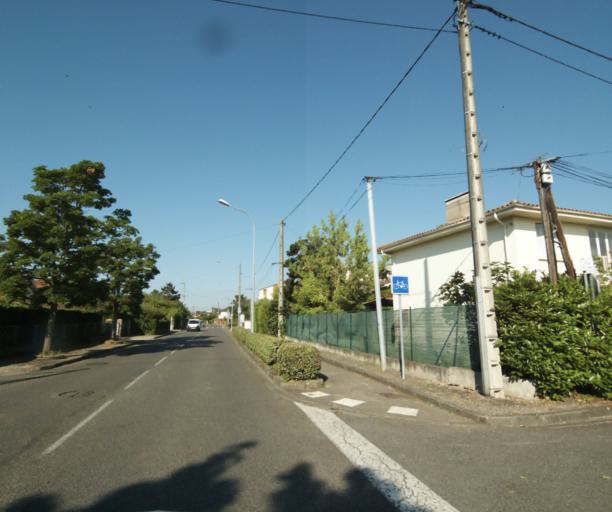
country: FR
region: Midi-Pyrenees
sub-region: Departement du Tarn-et-Garonne
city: Montauban
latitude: 44.0207
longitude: 1.3756
